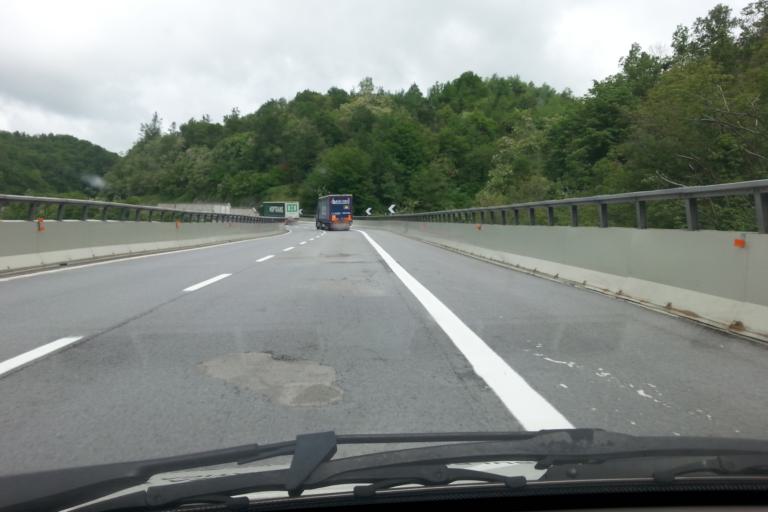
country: IT
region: Liguria
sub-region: Provincia di Savona
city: Valzemola
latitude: 44.3598
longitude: 8.1633
